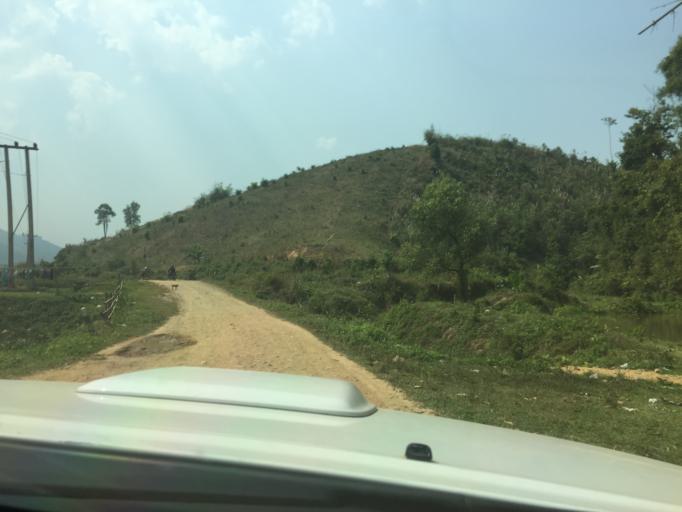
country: TH
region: Nan
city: Thung Chang
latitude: 19.7283
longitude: 100.7464
